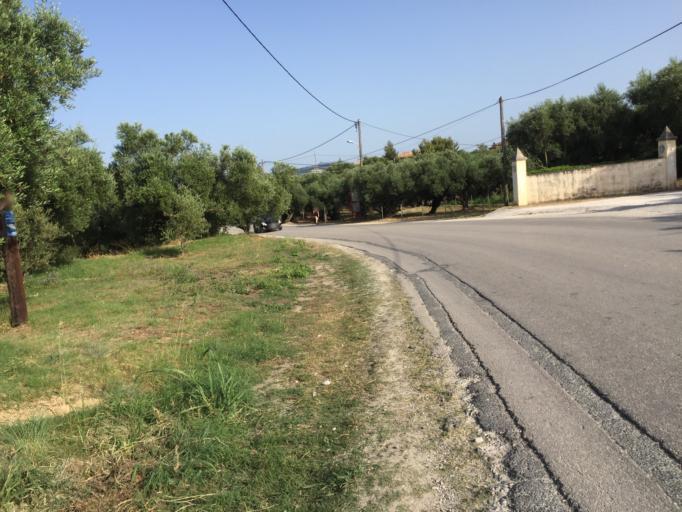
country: GR
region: Ionian Islands
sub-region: Nomos Zakynthou
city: Vanaton
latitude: 37.8218
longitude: 20.8544
